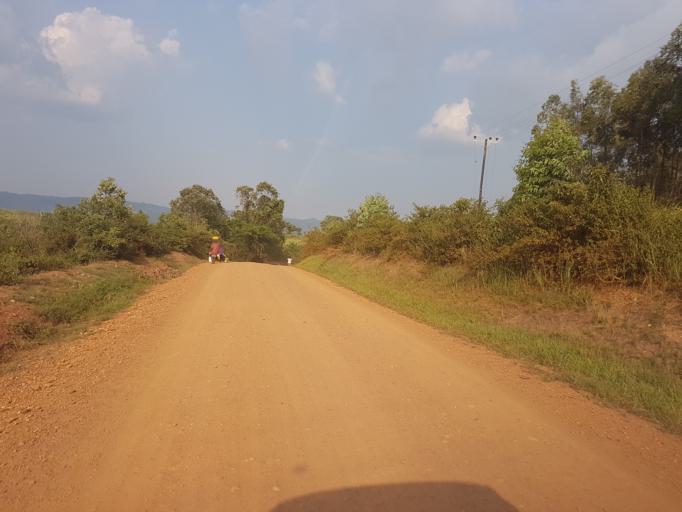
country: UG
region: Western Region
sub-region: Rukungiri District
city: Rukungiri
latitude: -0.6519
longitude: 29.8584
